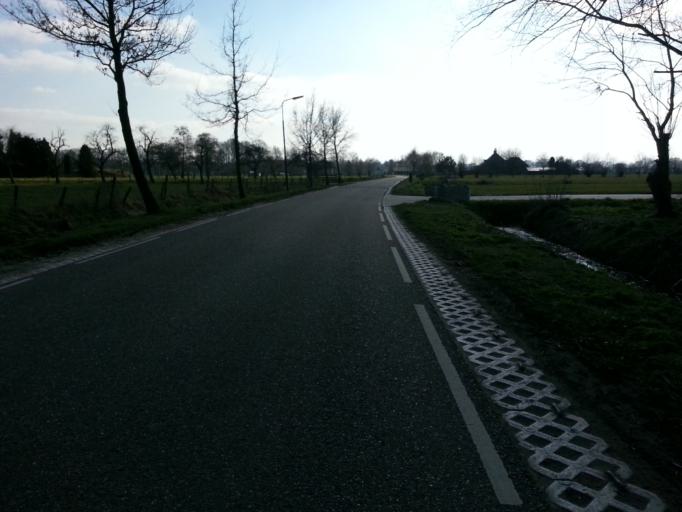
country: NL
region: Utrecht
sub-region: Gemeente Leusden
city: Leusden
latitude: 52.0988
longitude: 5.4517
